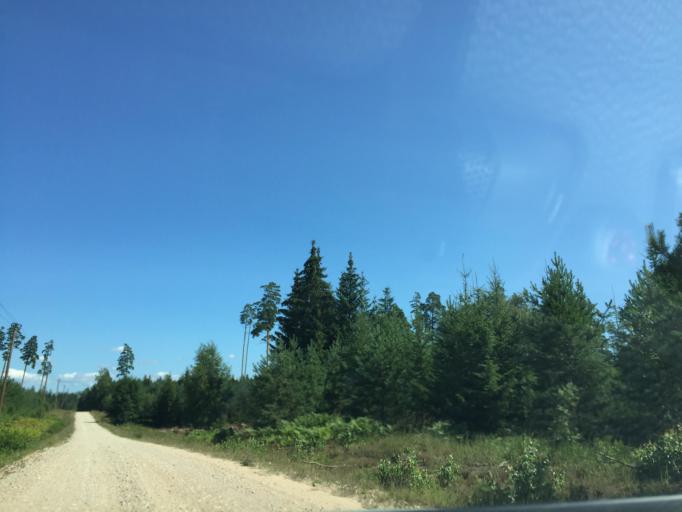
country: LV
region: Talsu Rajons
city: Stende
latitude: 57.1752
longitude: 22.3080
